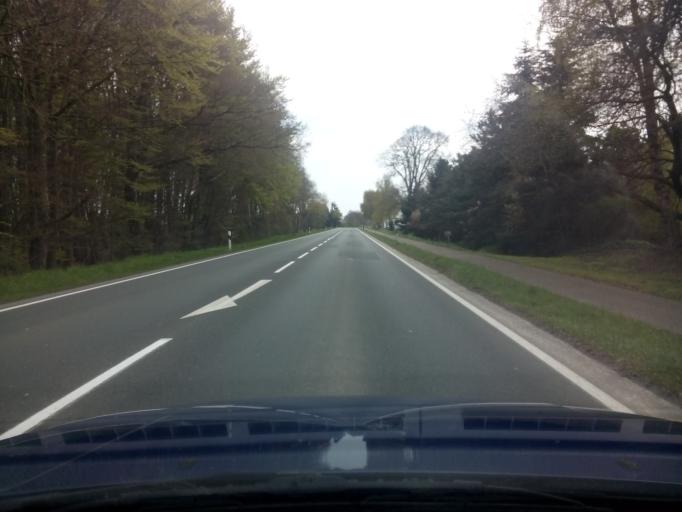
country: DE
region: Lower Saxony
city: Sustedt
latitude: 52.8594
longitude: 8.8846
